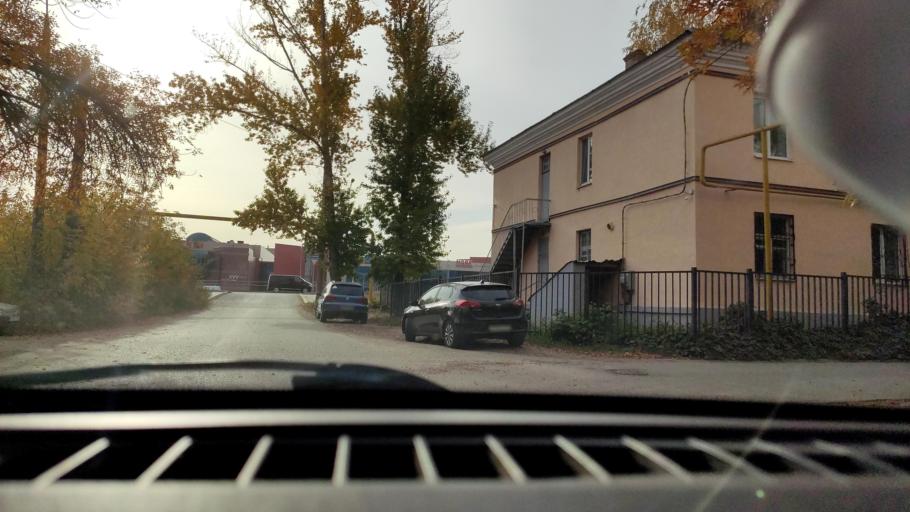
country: RU
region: Samara
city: Petra-Dubrava
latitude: 53.2781
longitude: 50.2689
